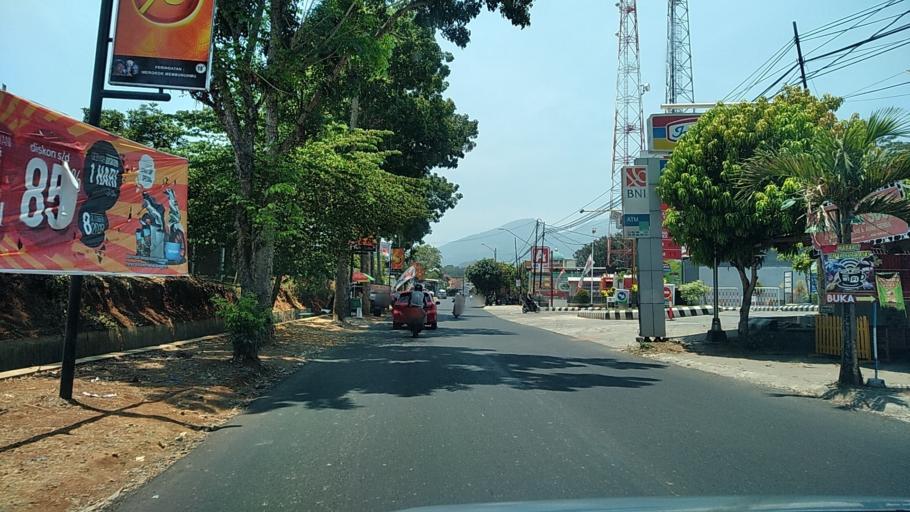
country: ID
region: Central Java
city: Ungaran
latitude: -7.0842
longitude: 110.3613
